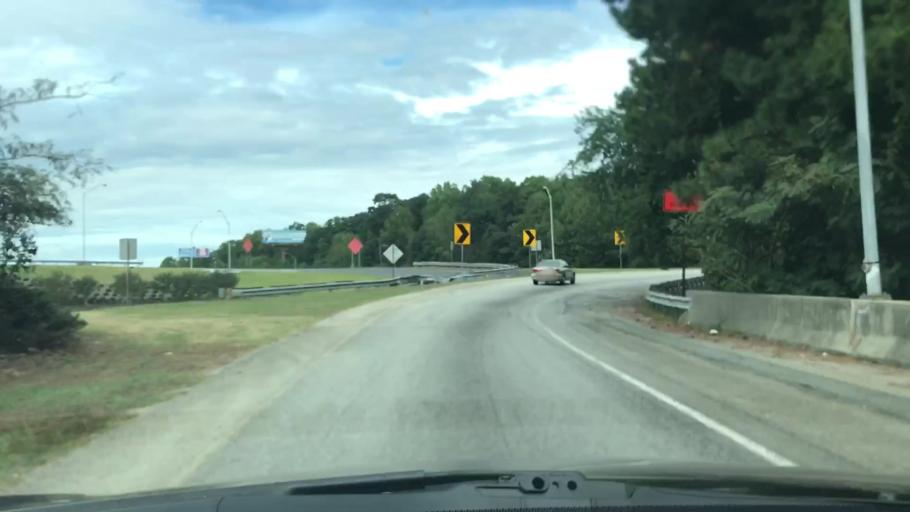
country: US
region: Georgia
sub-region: Cobb County
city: Fair Oaks
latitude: 33.9408
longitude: -84.5025
